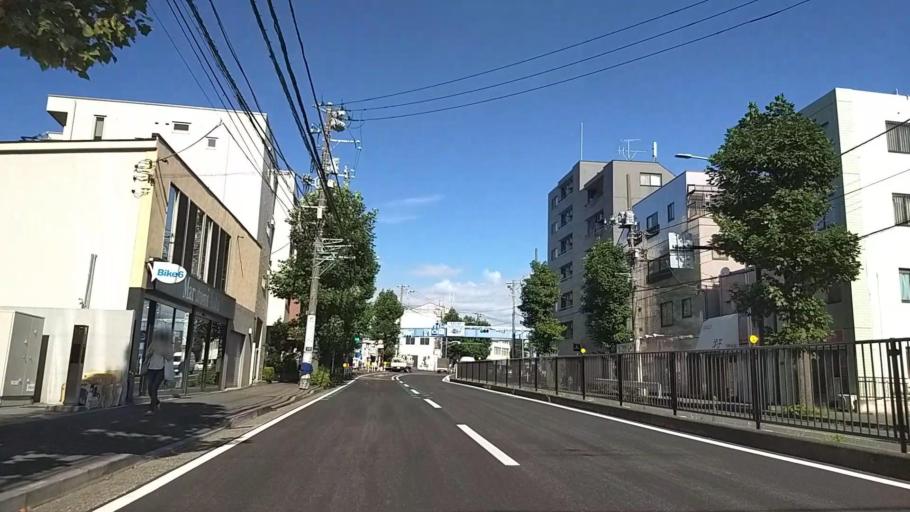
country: JP
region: Kanagawa
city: Yokohama
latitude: 35.4899
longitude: 139.6222
